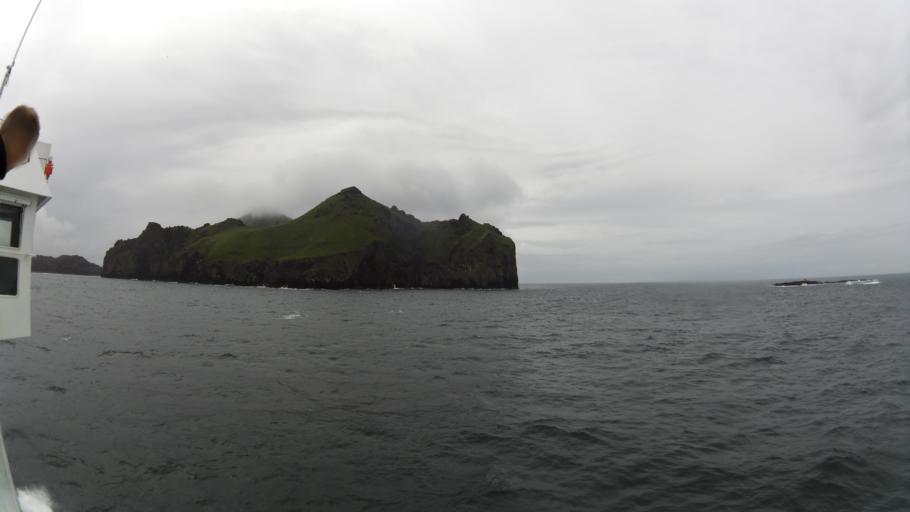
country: IS
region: South
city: Vestmannaeyjar
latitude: 63.4542
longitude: -20.2291
